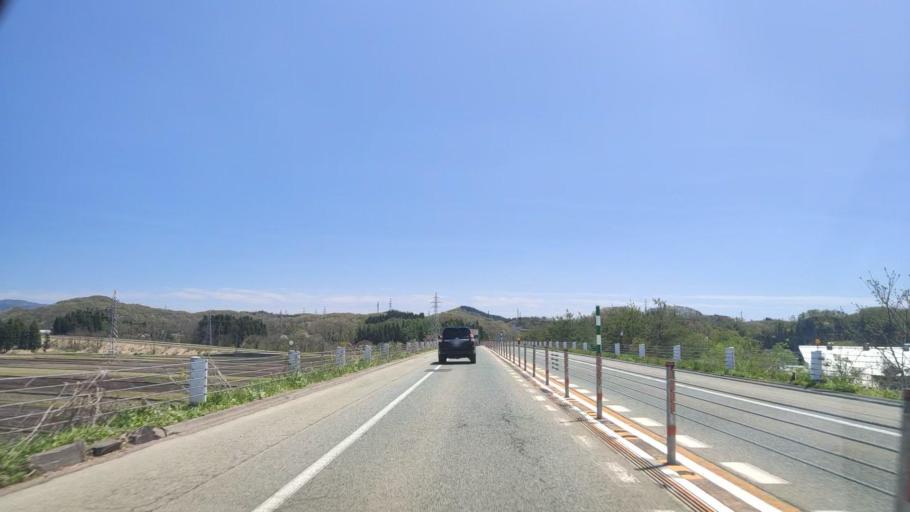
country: JP
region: Yamagata
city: Shinjo
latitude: 38.7329
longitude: 140.3031
